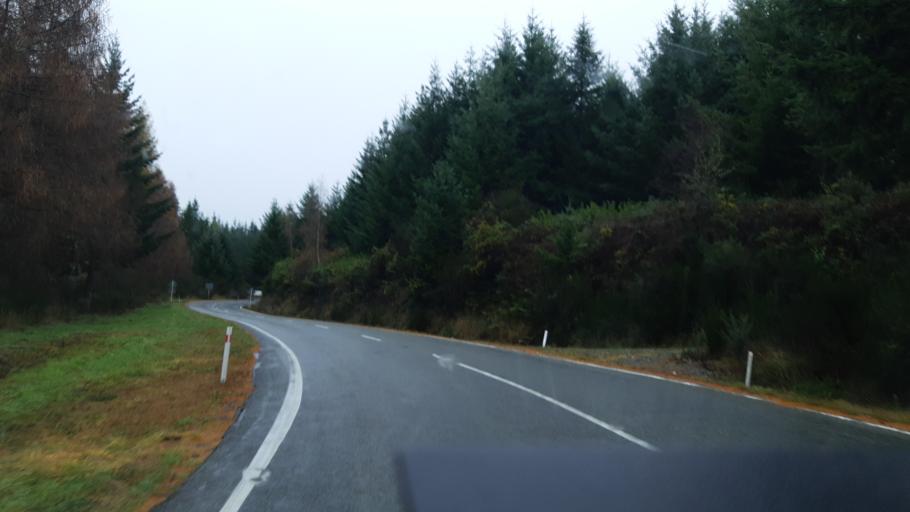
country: NZ
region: Tasman
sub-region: Tasman District
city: Wakefield
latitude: -41.6677
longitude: 172.8742
